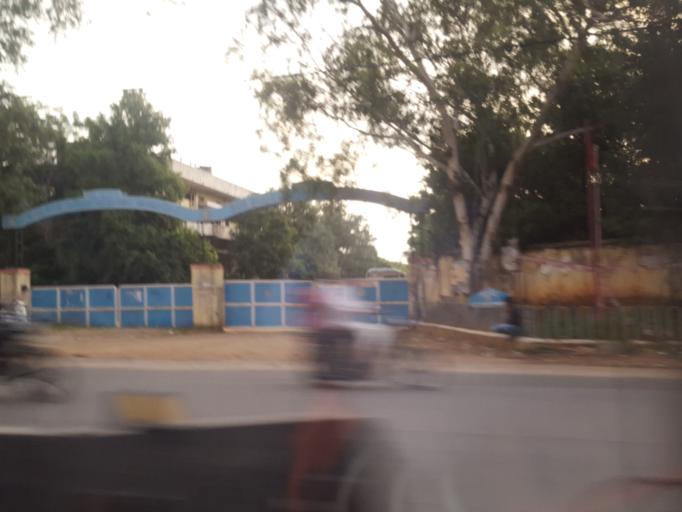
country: IN
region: Telangana
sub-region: Rangareddi
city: Kukatpalli
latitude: 17.5123
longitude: 78.3612
